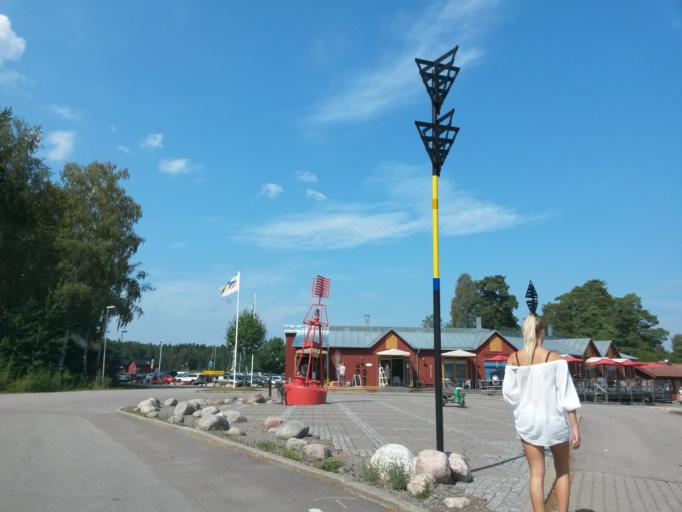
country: SE
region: Vaestra Goetaland
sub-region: Lidkopings Kommun
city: Lidkoping
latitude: 58.6898
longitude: 13.2007
